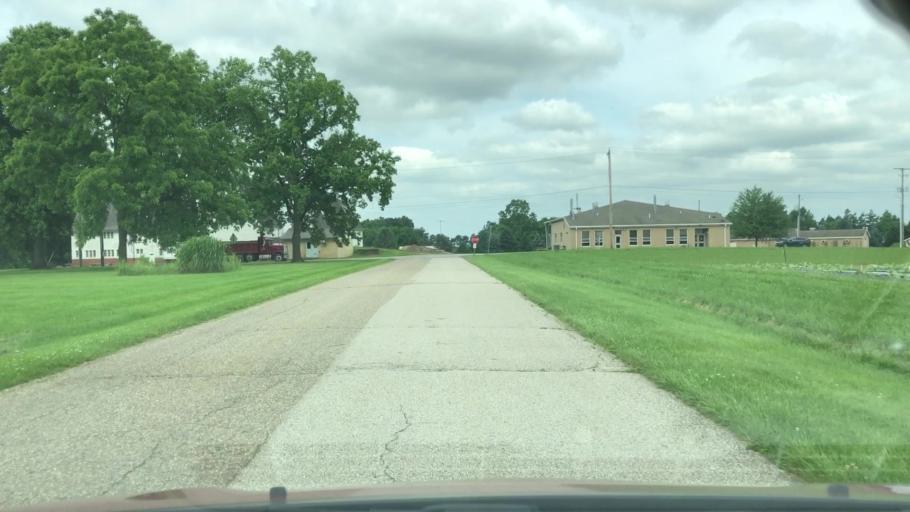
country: US
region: Ohio
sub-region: Wayne County
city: Wooster
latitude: 40.7712
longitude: -81.9099
